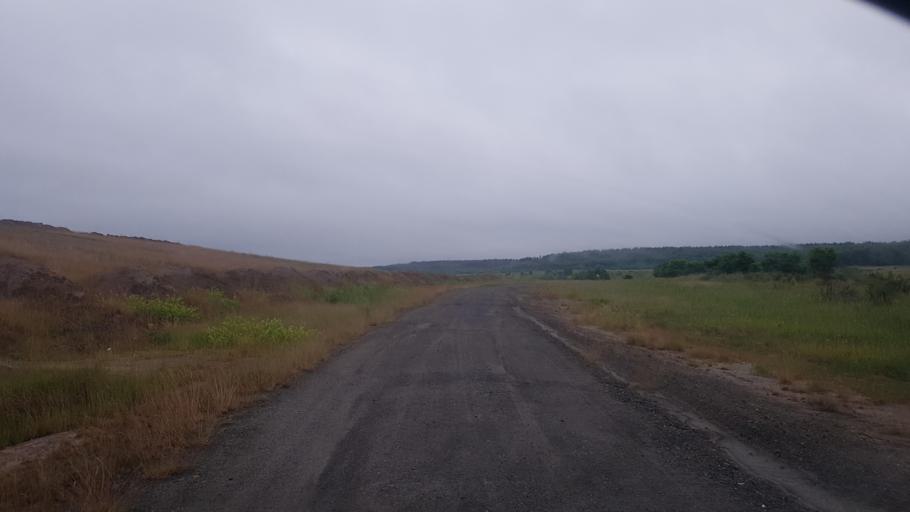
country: DE
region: Brandenburg
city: Lauchhammer
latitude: 51.5337
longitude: 13.7407
